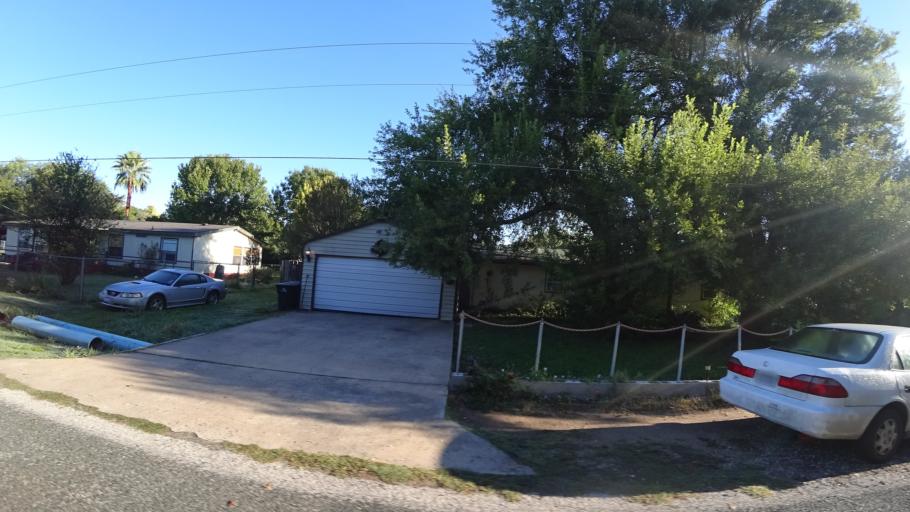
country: US
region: Texas
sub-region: Travis County
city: Hornsby Bend
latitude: 30.2238
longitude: -97.6288
